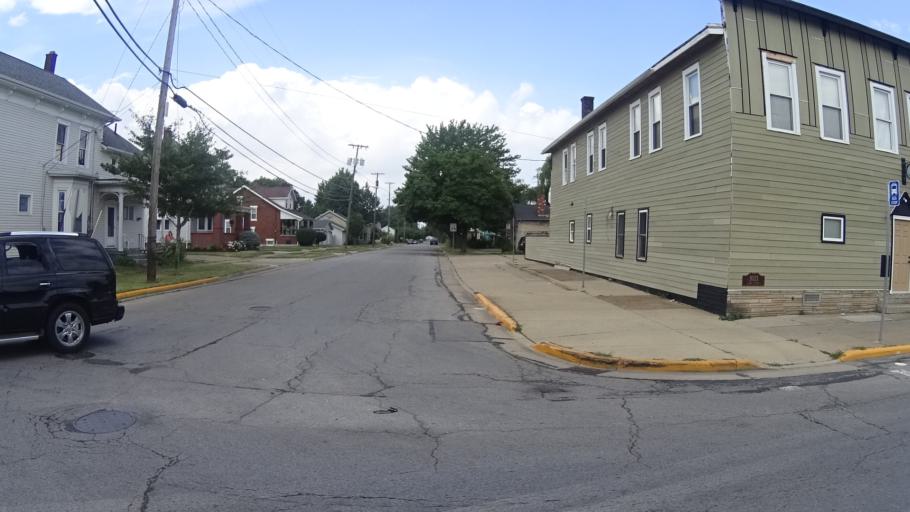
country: US
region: Ohio
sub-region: Erie County
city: Sandusky
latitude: 41.4454
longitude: -82.7204
